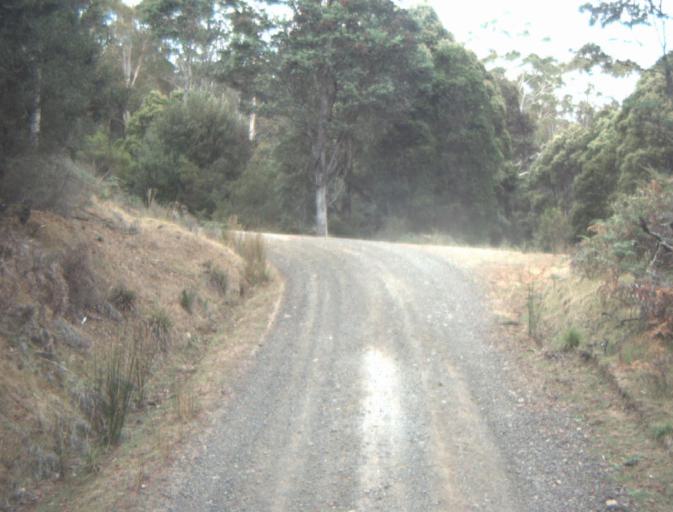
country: AU
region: Tasmania
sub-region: Launceston
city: Mayfield
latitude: -41.2805
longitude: 147.2336
